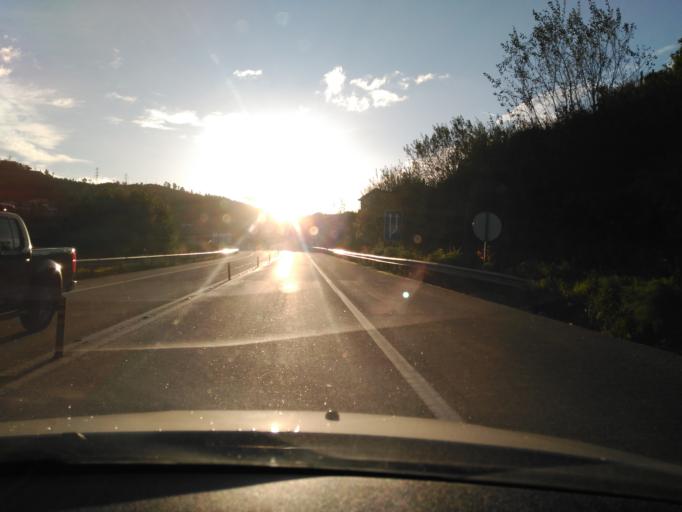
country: PT
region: Braga
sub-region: Fafe
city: Aroes
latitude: 41.4451
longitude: -8.2543
